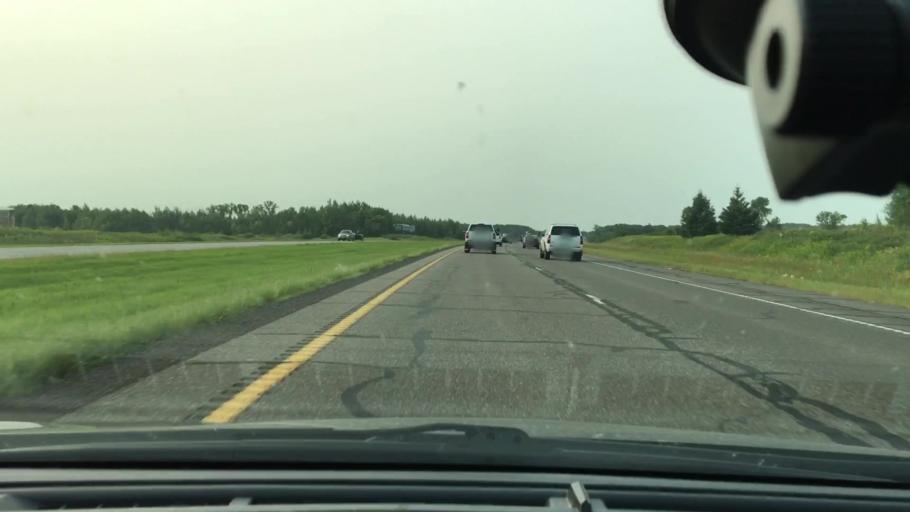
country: US
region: Minnesota
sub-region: Mille Lacs County
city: Milaca
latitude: 45.7687
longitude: -93.6443
